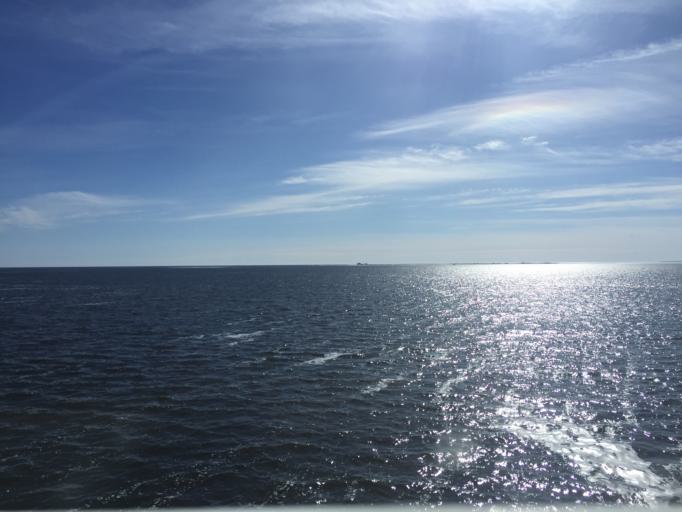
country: EE
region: Saare
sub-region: Orissaare vald
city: Orissaare
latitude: 58.5755
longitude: 23.4430
